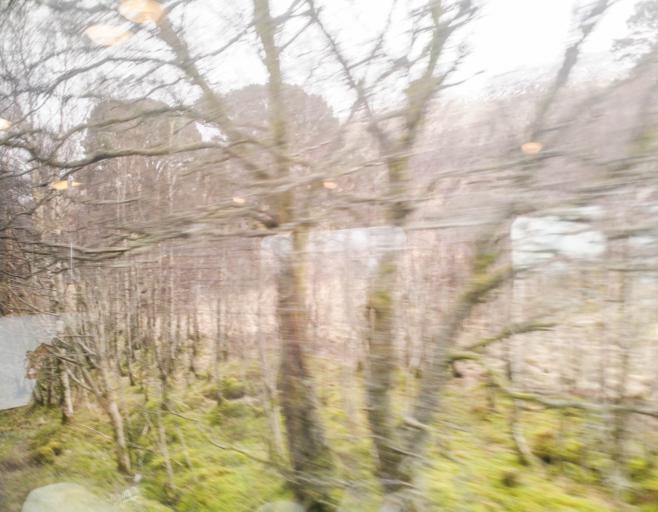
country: GB
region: Scotland
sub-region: Highland
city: Spean Bridge
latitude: 56.5703
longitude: -4.6928
